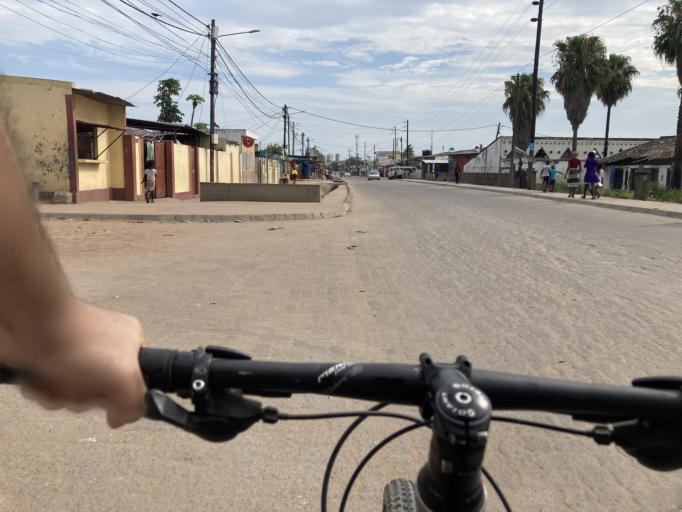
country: MZ
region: Maputo City
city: Maputo
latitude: -25.9454
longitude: 32.5827
